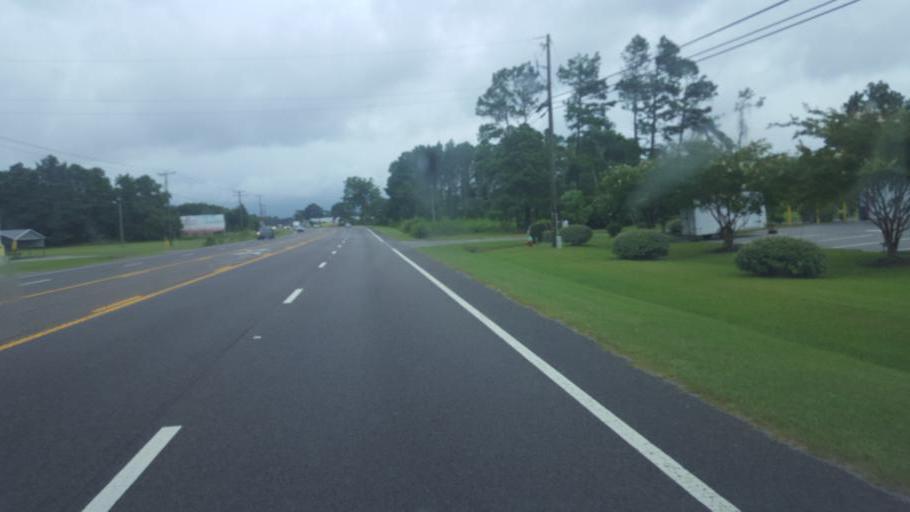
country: US
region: North Carolina
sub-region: Dare County
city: Southern Shores
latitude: 36.1378
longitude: -75.8404
